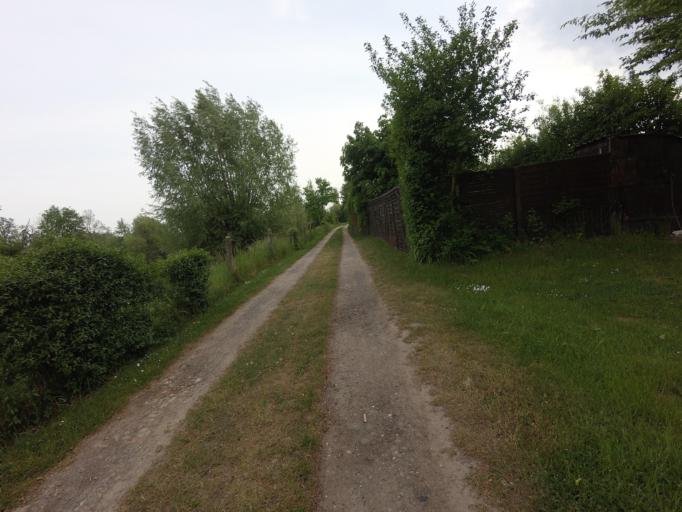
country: DE
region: Lower Saxony
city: Nordstemmen
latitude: 52.1586
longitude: 9.7577
